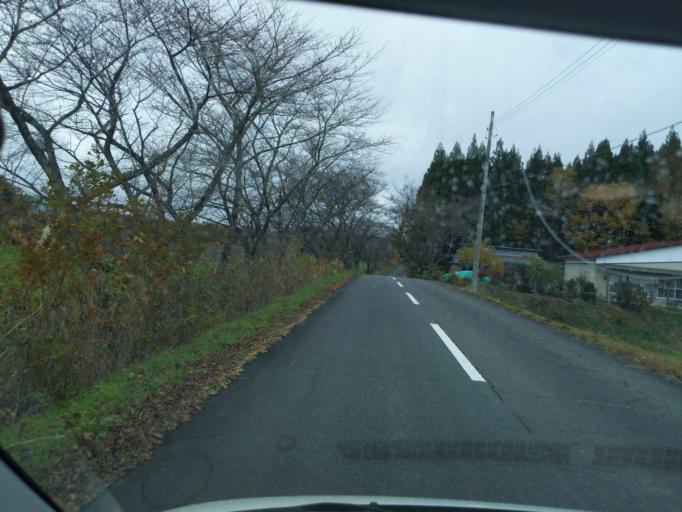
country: JP
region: Iwate
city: Mizusawa
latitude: 39.0532
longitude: 141.0618
